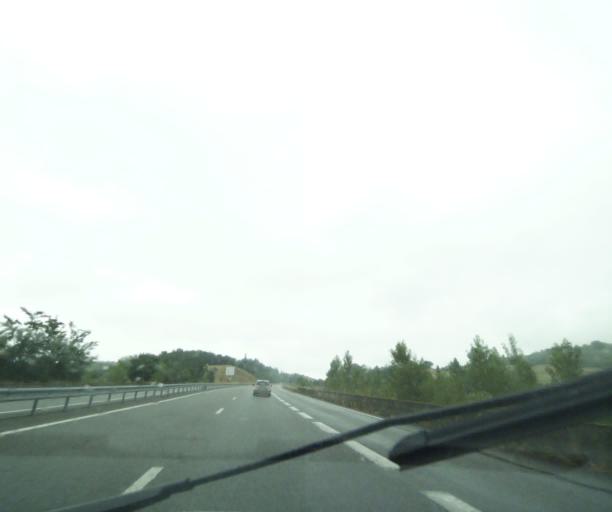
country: FR
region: Midi-Pyrenees
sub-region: Departement du Tarn
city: Le Garric
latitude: 44.0023
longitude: 2.1722
